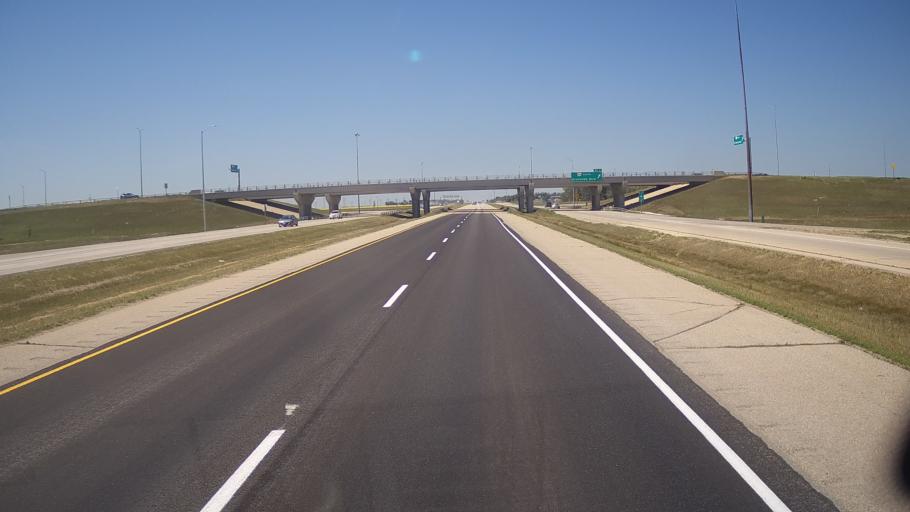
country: CA
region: Manitoba
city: Winnipeg
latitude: 49.9900
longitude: -97.2265
